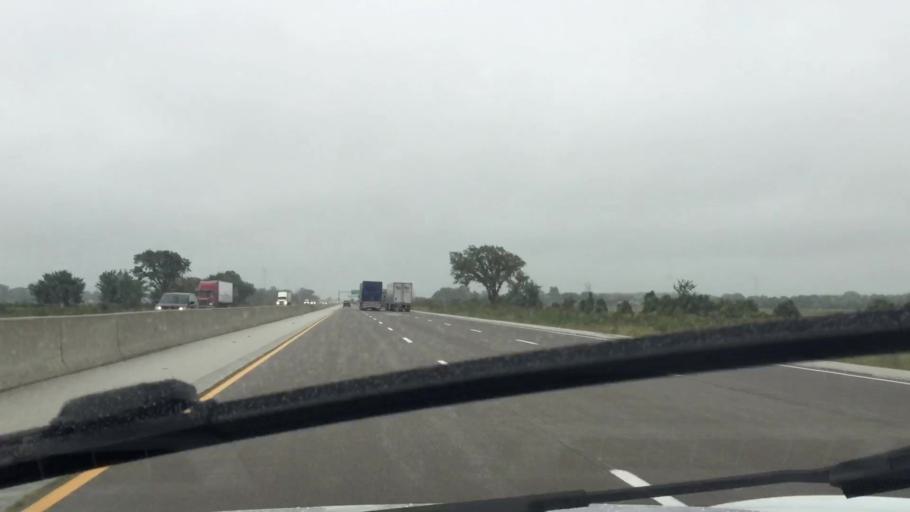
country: US
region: Michigan
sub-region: Wayne County
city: Grosse Pointe
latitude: 42.2371
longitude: -82.7316
